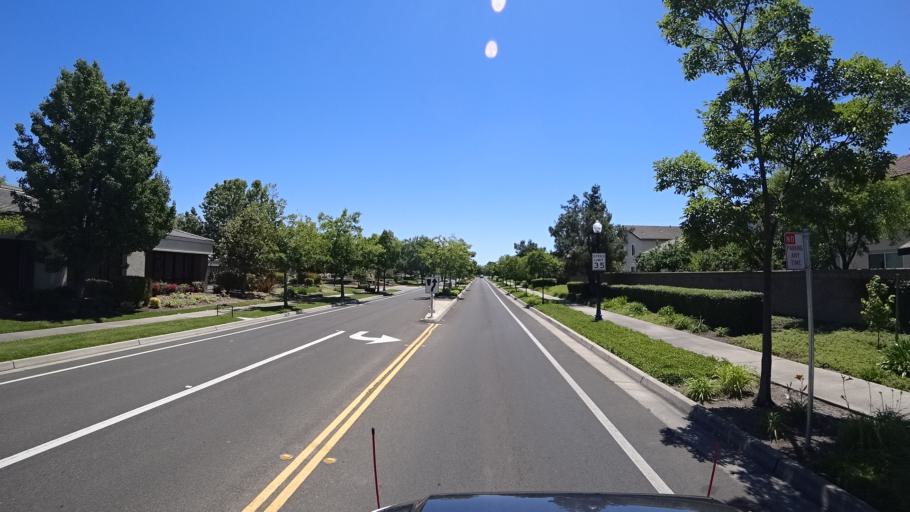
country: US
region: California
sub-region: Yolo County
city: West Sacramento
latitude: 38.6514
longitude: -121.5328
